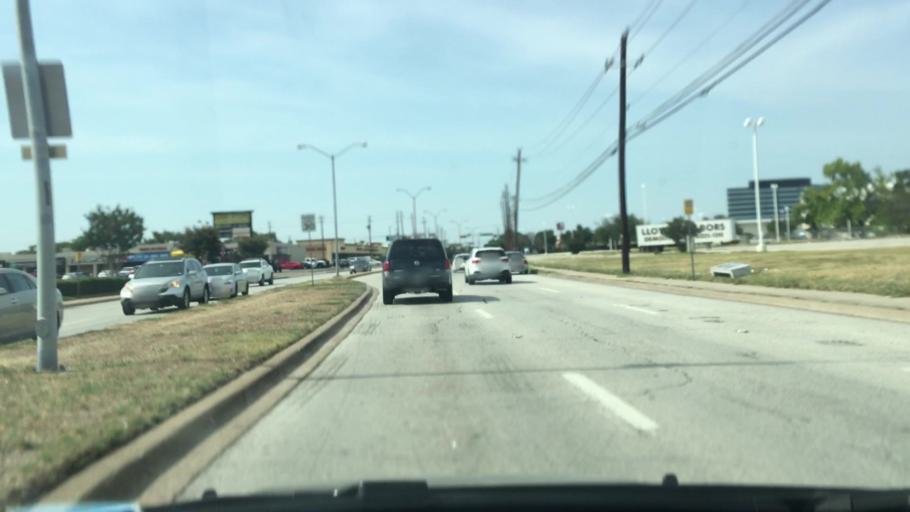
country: US
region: Texas
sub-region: Dallas County
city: Addison
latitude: 32.9273
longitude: -96.8112
